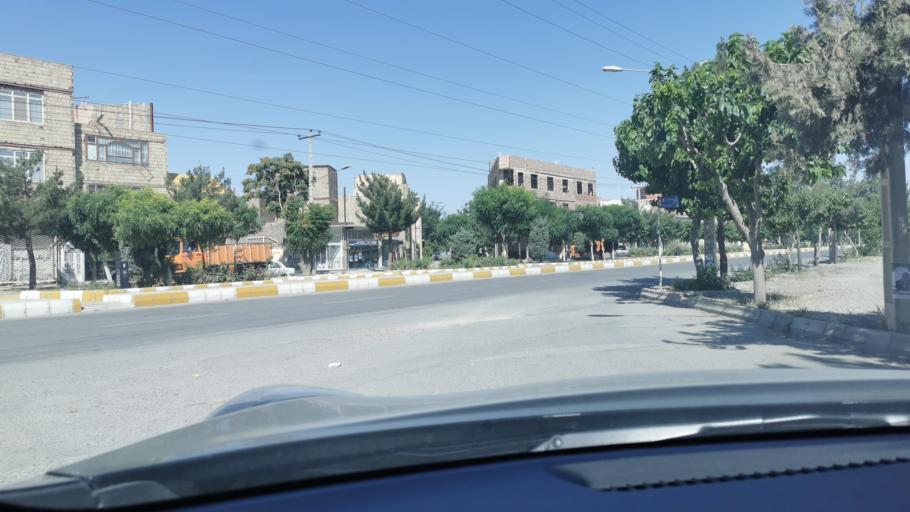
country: IR
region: Razavi Khorasan
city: Chenaran
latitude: 36.6388
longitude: 59.1177
